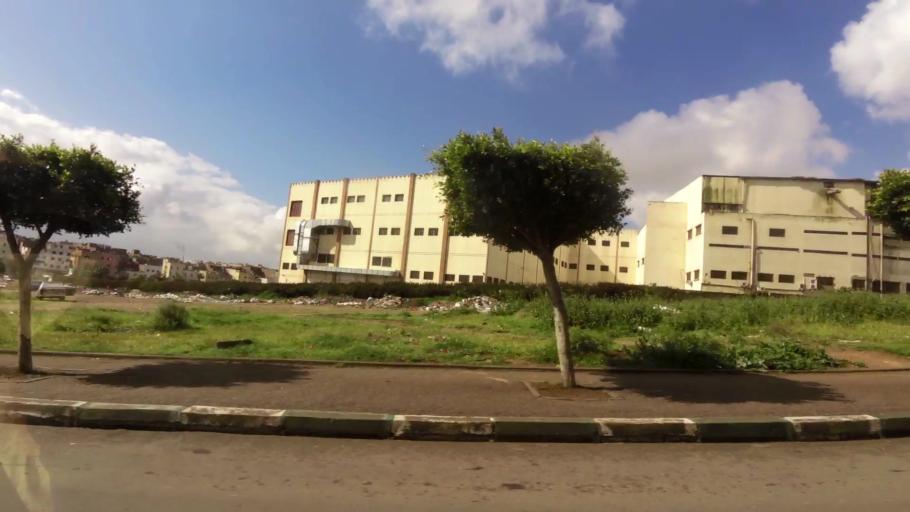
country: MA
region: Grand Casablanca
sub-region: Nouaceur
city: Bouskoura
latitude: 33.5316
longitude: -7.6773
